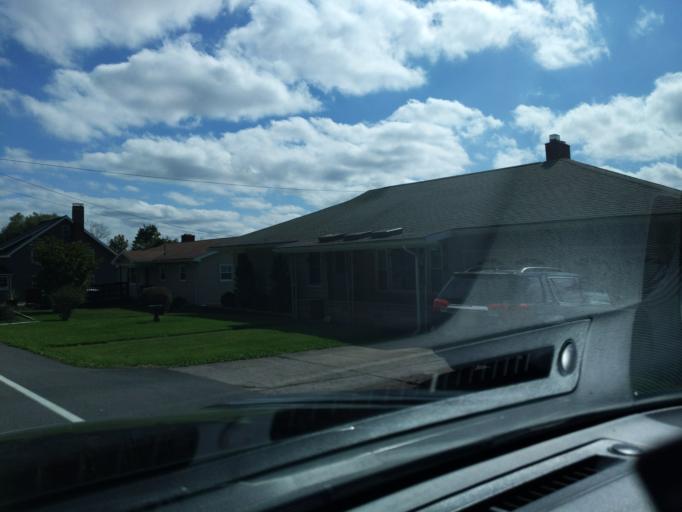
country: US
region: Pennsylvania
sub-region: Blair County
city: Altoona
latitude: 40.4932
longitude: -78.4532
